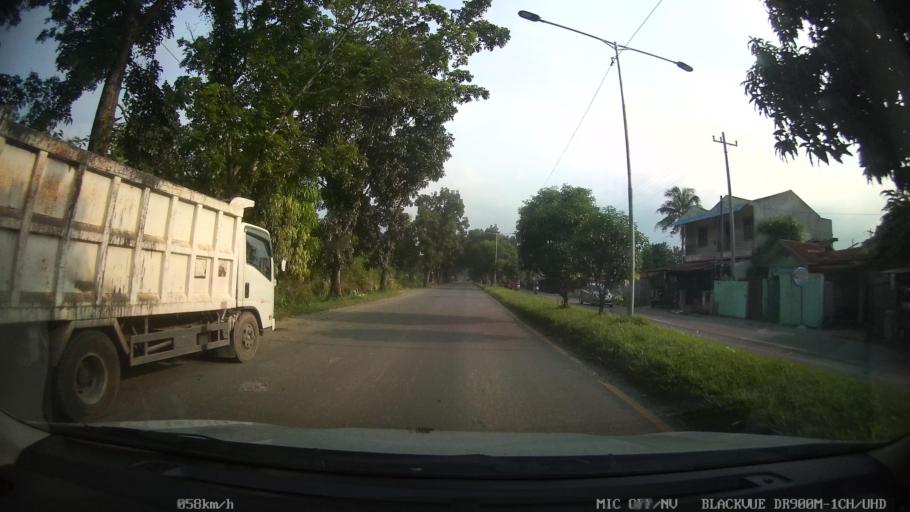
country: ID
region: North Sumatra
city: Binjai
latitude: 3.6148
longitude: 98.5345
